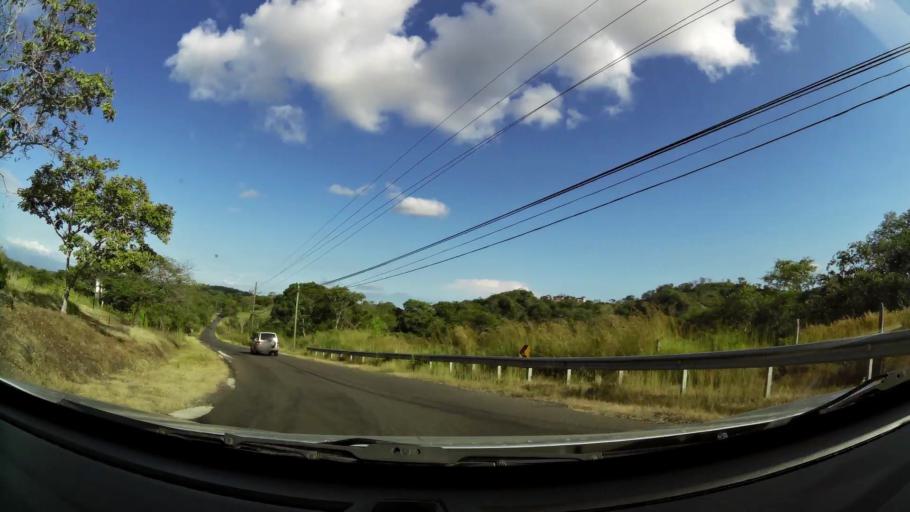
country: CR
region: Guanacaste
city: Sardinal
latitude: 10.5398
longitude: -85.6765
